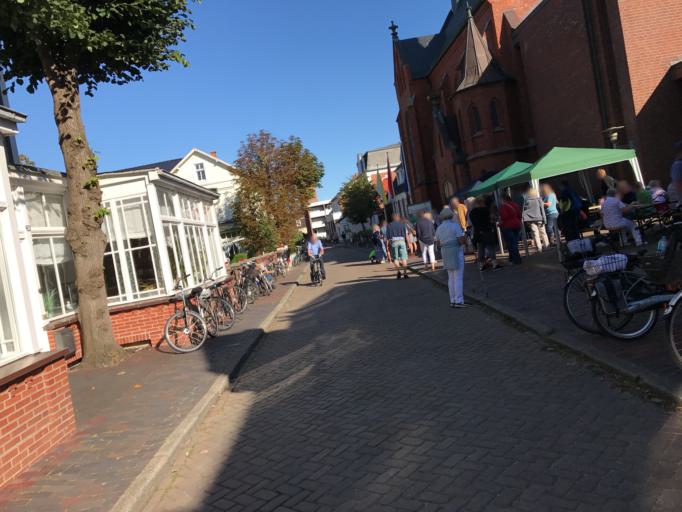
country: DE
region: Lower Saxony
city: Borkum
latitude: 53.5888
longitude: 6.6659
